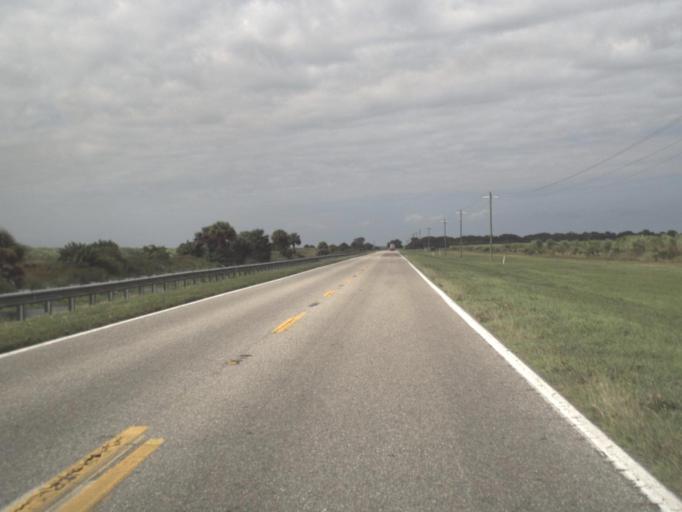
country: US
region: Florida
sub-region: Glades County
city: Moore Haven
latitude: 26.7527
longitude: -81.1332
